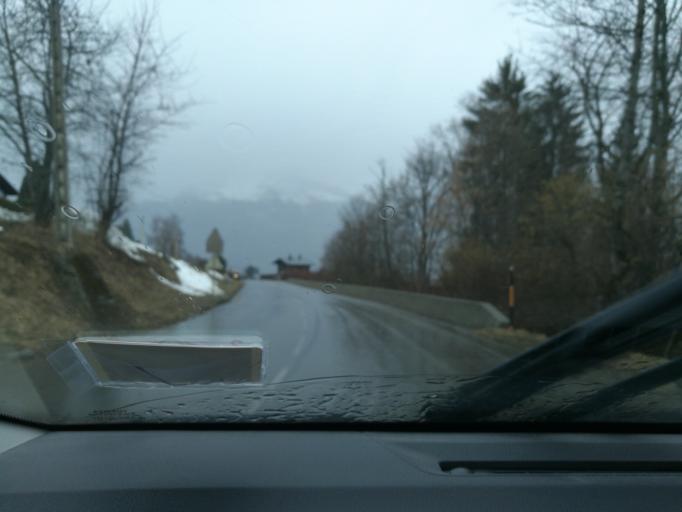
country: FR
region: Rhone-Alpes
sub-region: Departement de la Haute-Savoie
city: Saint-Gervais-les-Bains
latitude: 45.8842
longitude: 6.7039
